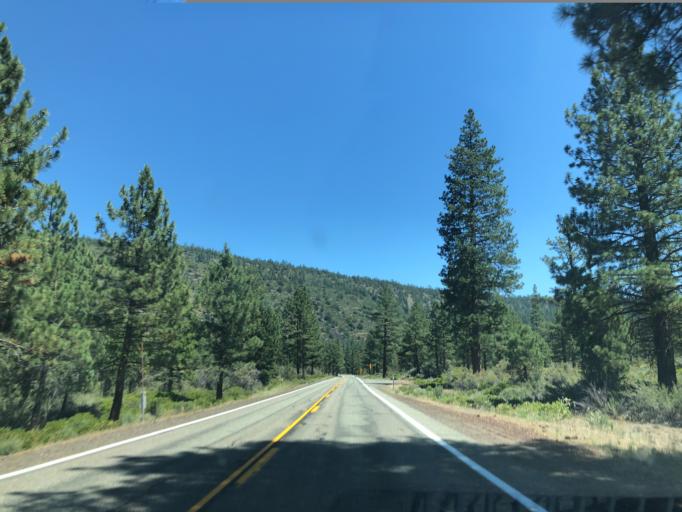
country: US
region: California
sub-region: Shasta County
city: Burney
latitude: 40.6777
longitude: -121.4103
